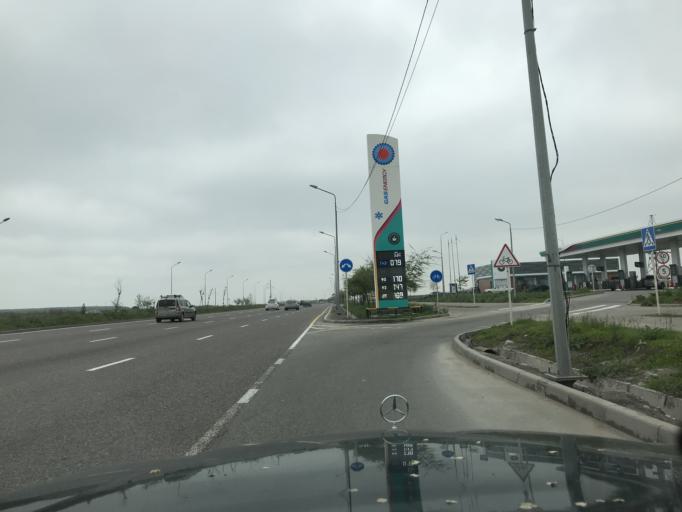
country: KZ
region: Almaty Oblysy
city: Burunday
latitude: 43.2950
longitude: 76.8322
